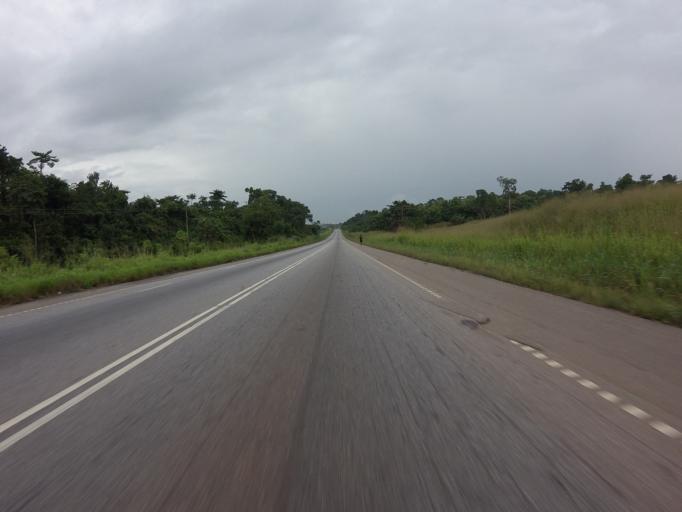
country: GH
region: Ashanti
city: Konongo
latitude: 6.6126
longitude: -1.2516
